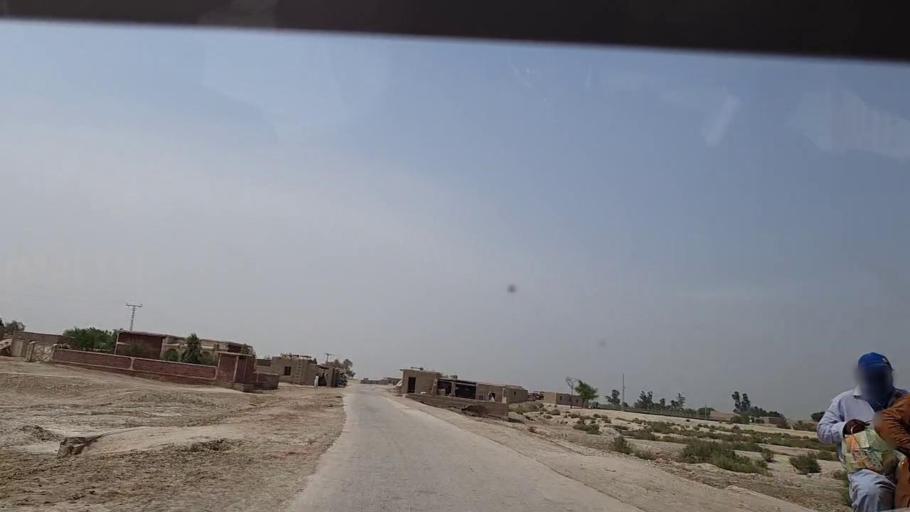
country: PK
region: Sindh
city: Khairpur Nathan Shah
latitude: 27.0727
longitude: 67.6514
